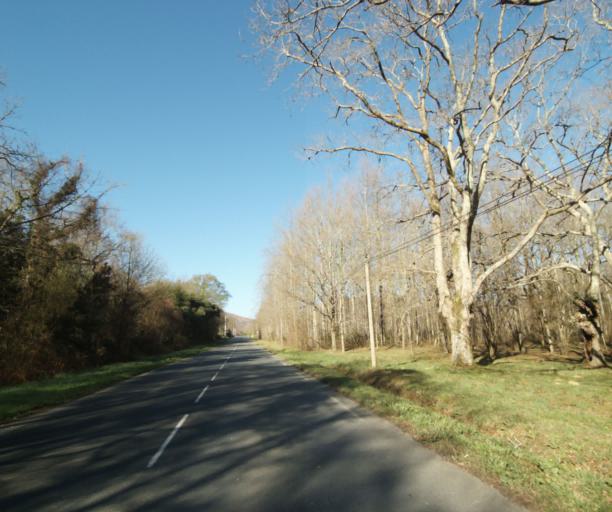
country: FR
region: Aquitaine
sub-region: Departement des Pyrenees-Atlantiques
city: Urrugne
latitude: 43.3342
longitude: -1.6813
